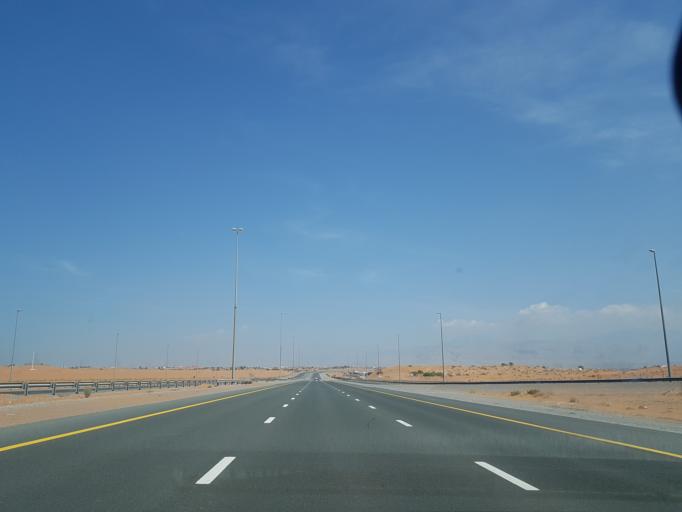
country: AE
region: Ra's al Khaymah
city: Ras al-Khaimah
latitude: 25.6954
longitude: 55.9258
